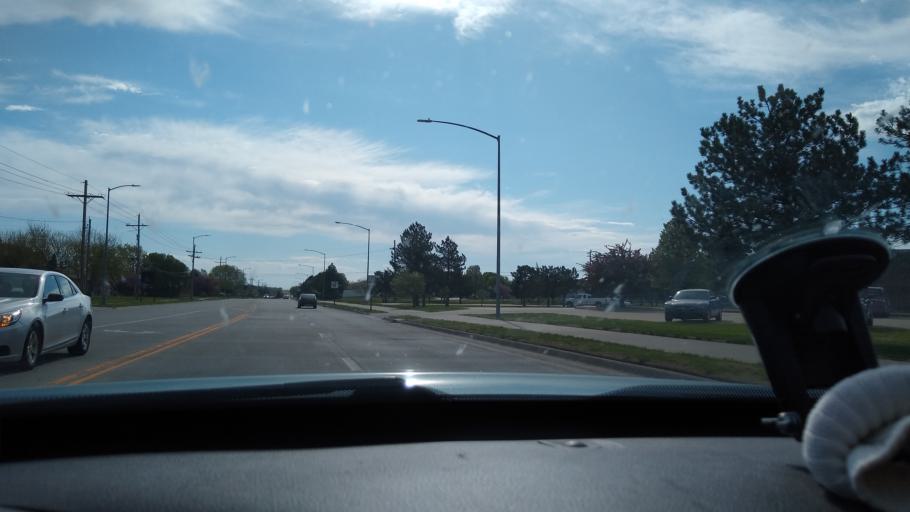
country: US
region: Kansas
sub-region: Saline County
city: Salina
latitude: 38.7980
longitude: -97.5938
